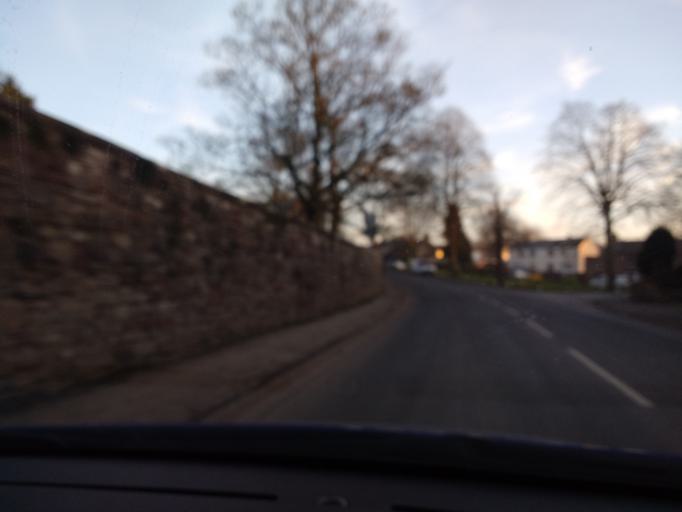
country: GB
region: England
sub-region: Cumbria
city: Appleby-in-Westmorland
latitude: 54.5734
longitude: -2.4904
